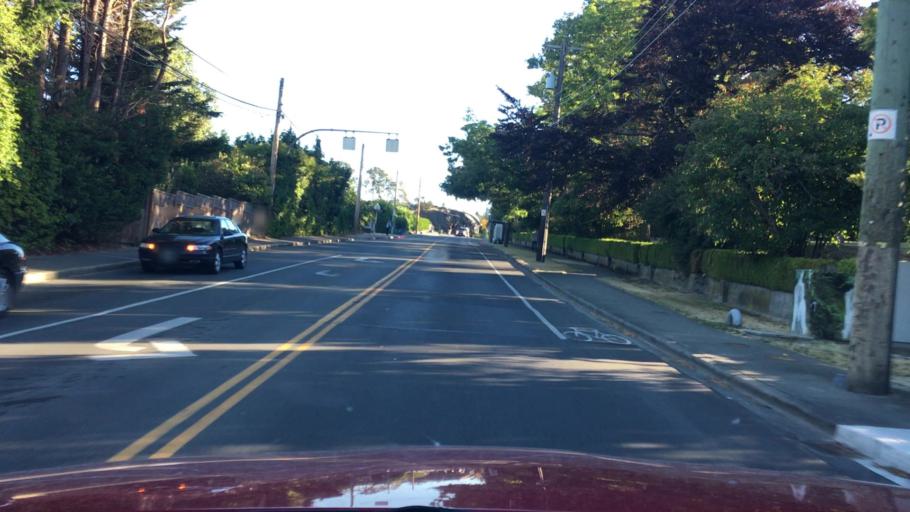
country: CA
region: British Columbia
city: Oak Bay
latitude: 48.4463
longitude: -123.3265
